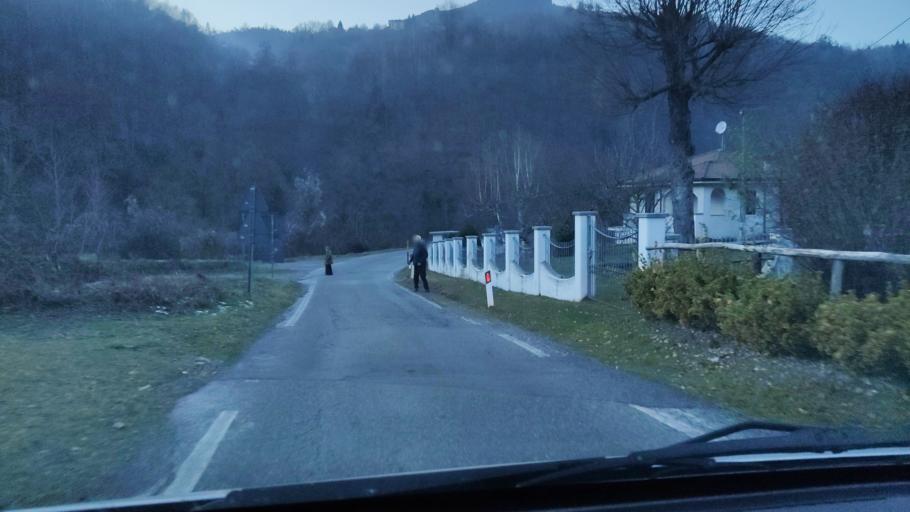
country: IT
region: Piedmont
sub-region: Provincia di Cuneo
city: Viola
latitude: 44.2876
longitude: 7.9772
